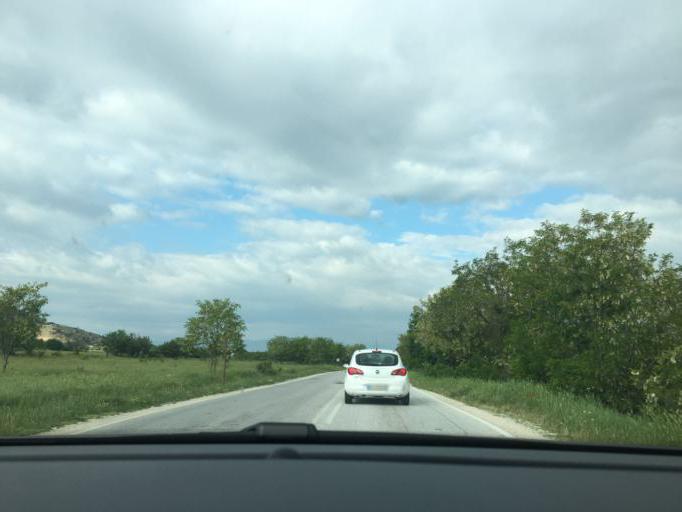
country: MK
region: Prilep
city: Prilep
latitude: 41.3637
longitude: 21.6047
